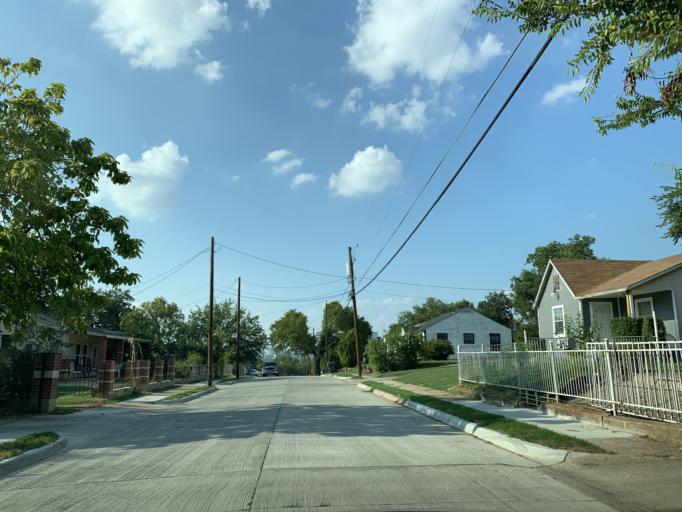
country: US
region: Texas
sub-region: Dallas County
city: Dallas
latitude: 32.7447
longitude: -96.7937
